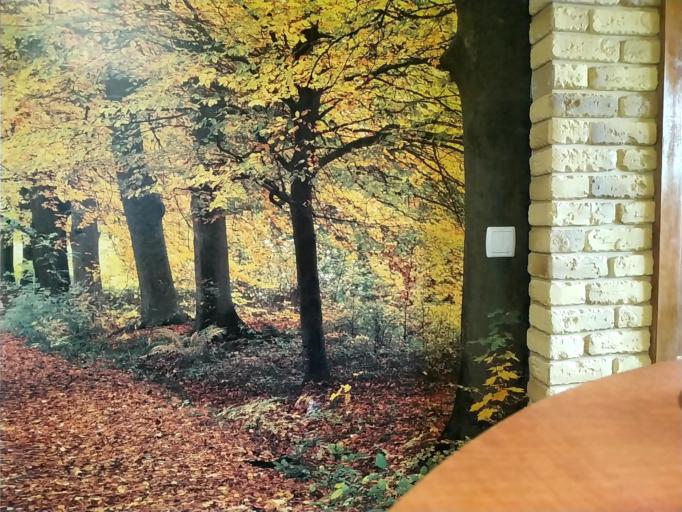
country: RU
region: Novgorod
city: Opechenskiy Posad
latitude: 58.2676
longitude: 34.0238
